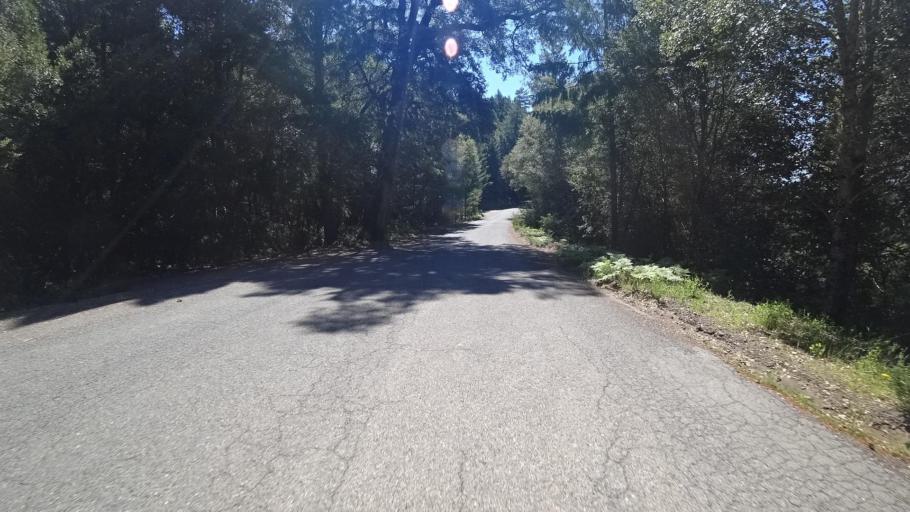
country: US
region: California
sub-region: Humboldt County
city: Redway
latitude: 40.1247
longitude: -123.9715
